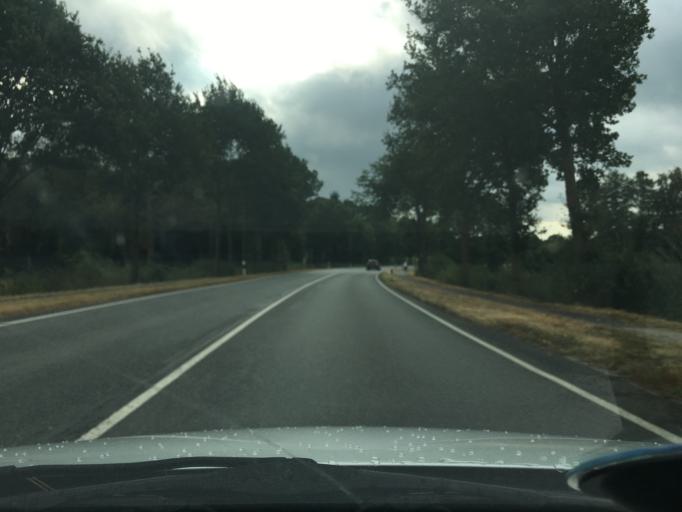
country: DE
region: Lower Saxony
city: Alfhausen
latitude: 52.4621
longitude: 7.9622
